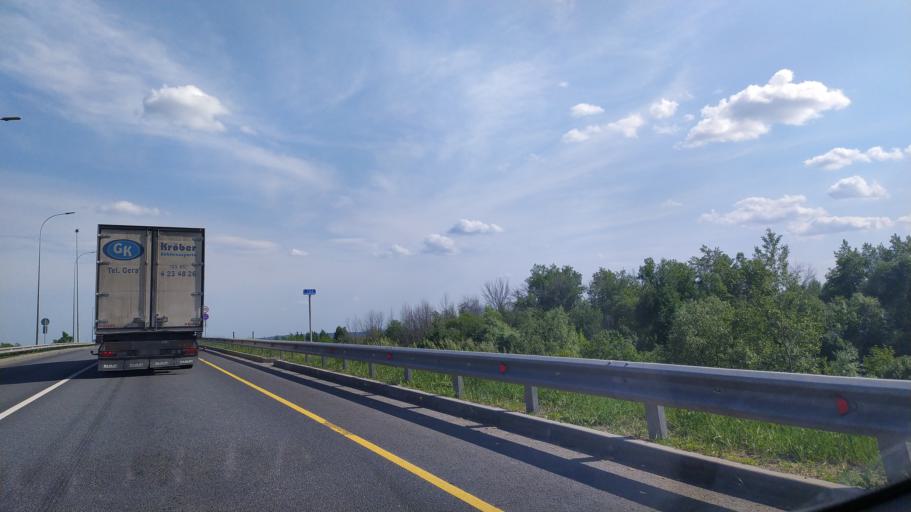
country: RU
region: Chuvashia
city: Kozlovka
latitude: 55.7551
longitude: 48.2057
